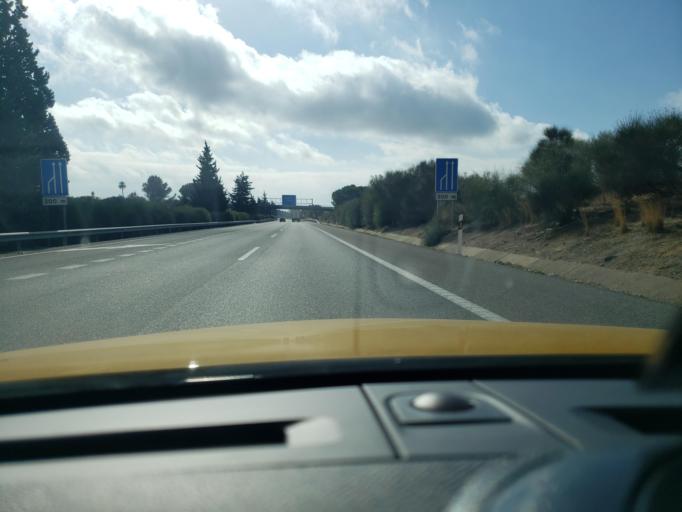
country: ES
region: Andalusia
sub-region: Provincia de Sevilla
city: Dos Hermanas
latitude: 37.2356
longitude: -5.9113
